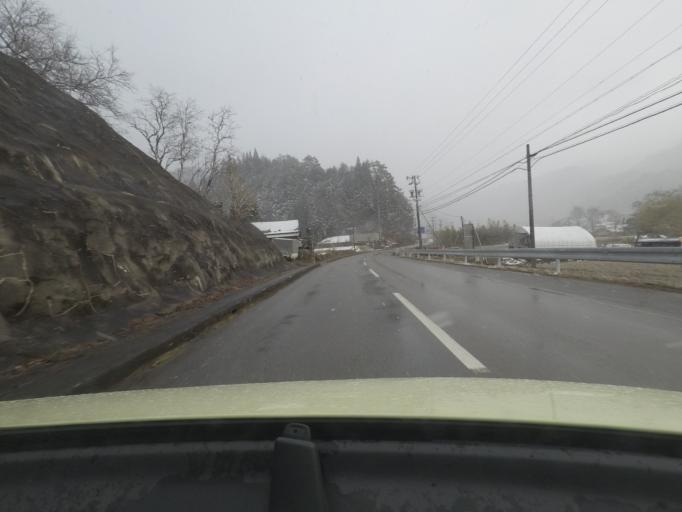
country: JP
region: Gifu
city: Takayama
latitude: 36.1407
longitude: 137.3109
